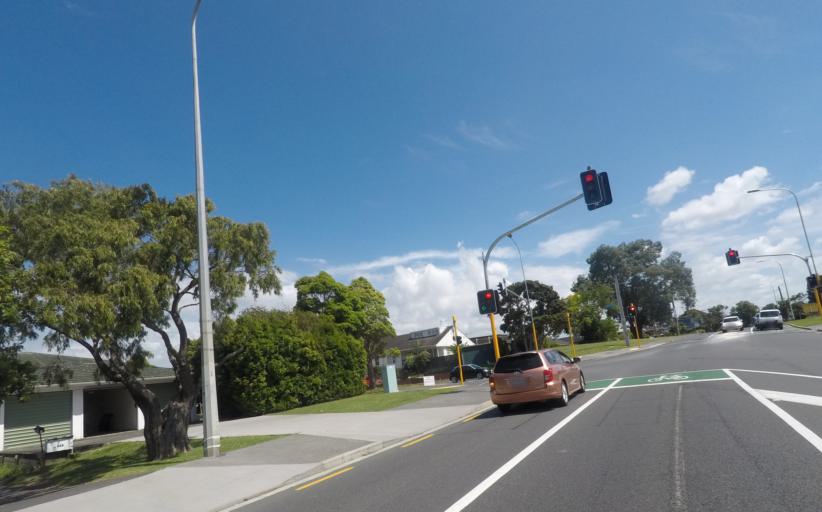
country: NZ
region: Auckland
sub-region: Auckland
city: Tamaki
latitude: -36.8709
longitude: 174.8453
